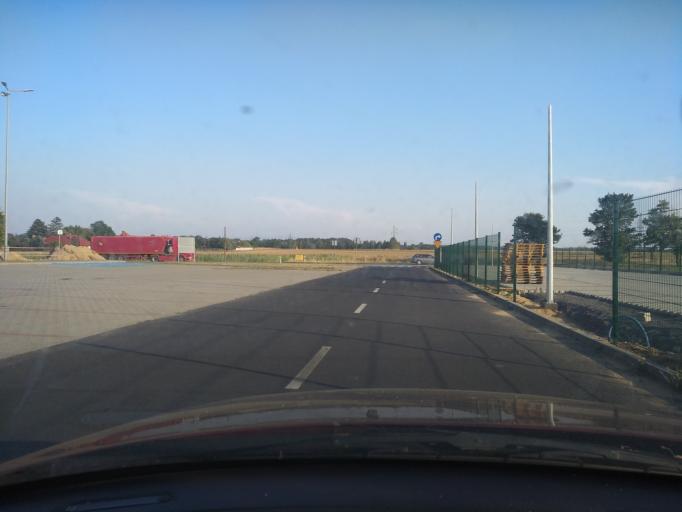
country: PL
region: Lower Silesian Voivodeship
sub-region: Powiat zgorzelecki
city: Lagow
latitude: 51.1575
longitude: 15.0389
